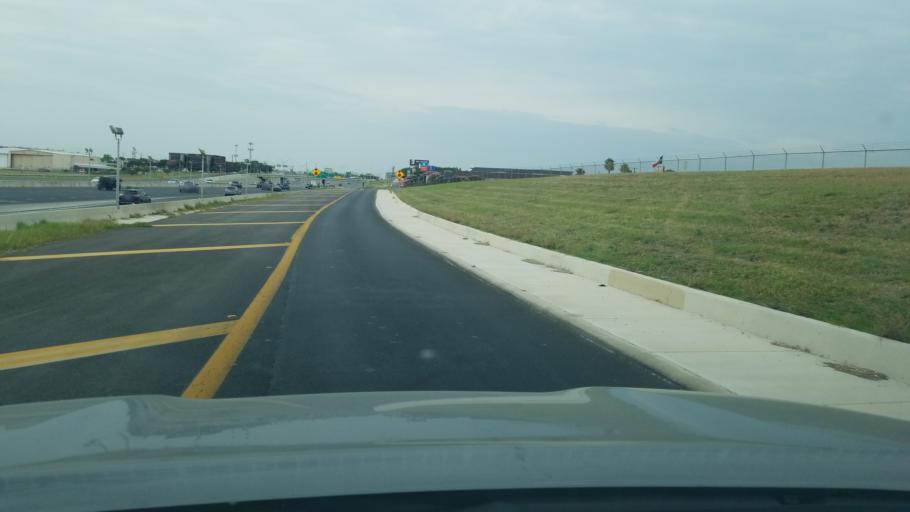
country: US
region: Texas
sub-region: Bexar County
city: Castle Hills
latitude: 29.5464
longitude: -98.4901
